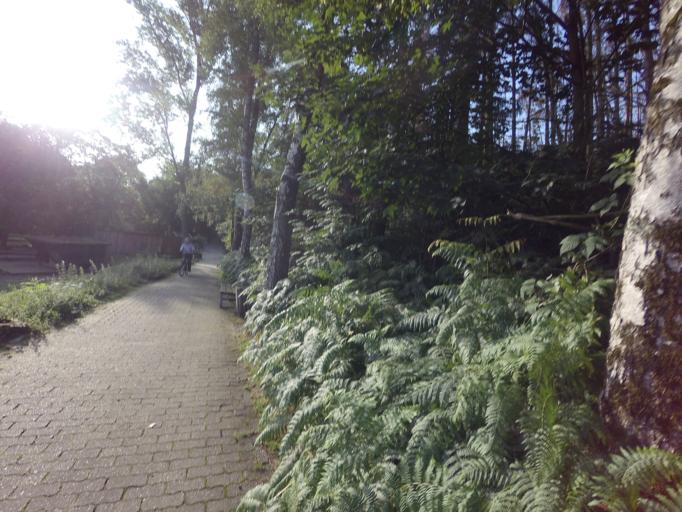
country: DE
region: North Rhine-Westphalia
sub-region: Regierungsbezirk Koln
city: Alsdorf
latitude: 50.8622
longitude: 6.1468
